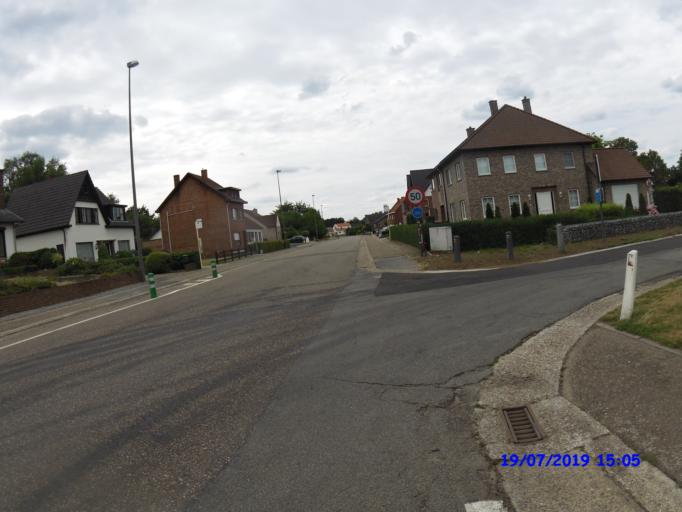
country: BE
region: Flanders
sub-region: Provincie Limburg
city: Hasselt
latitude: 50.9487
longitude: 5.3216
